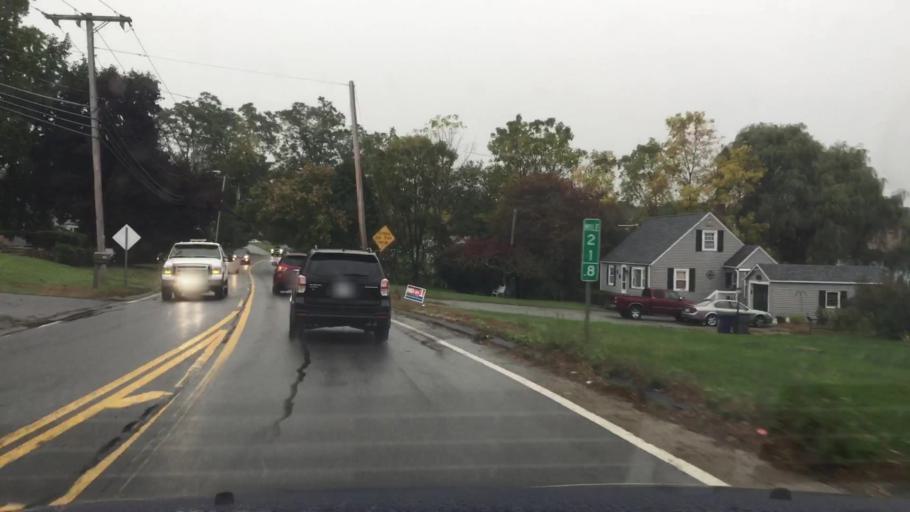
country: US
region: Massachusetts
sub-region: Middlesex County
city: Dracut
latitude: 42.6762
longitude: -71.2943
